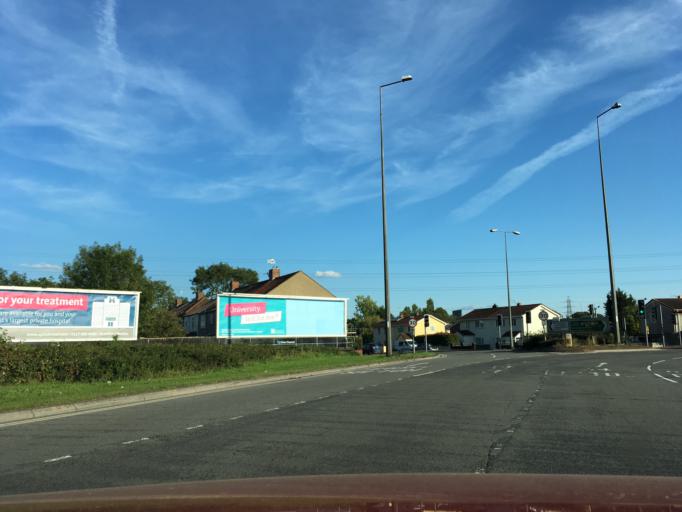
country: GB
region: England
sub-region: North Somerset
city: Easton-in-Gordano
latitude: 51.4982
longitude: -2.6899
